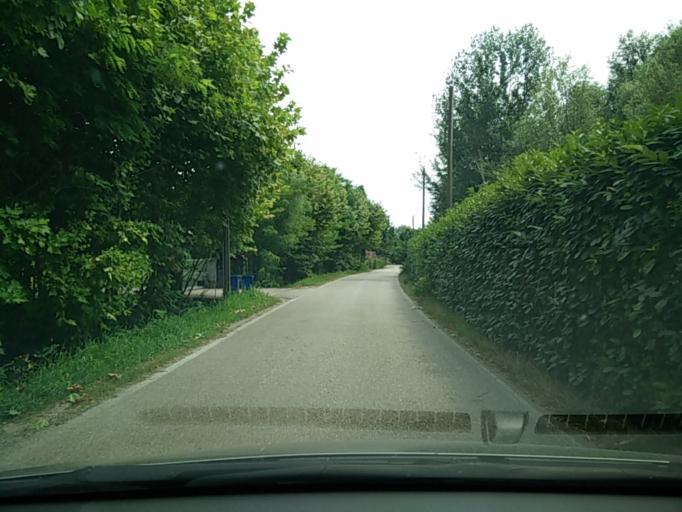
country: IT
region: Veneto
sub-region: Provincia di Treviso
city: Casier
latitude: 45.6477
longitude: 12.2882
